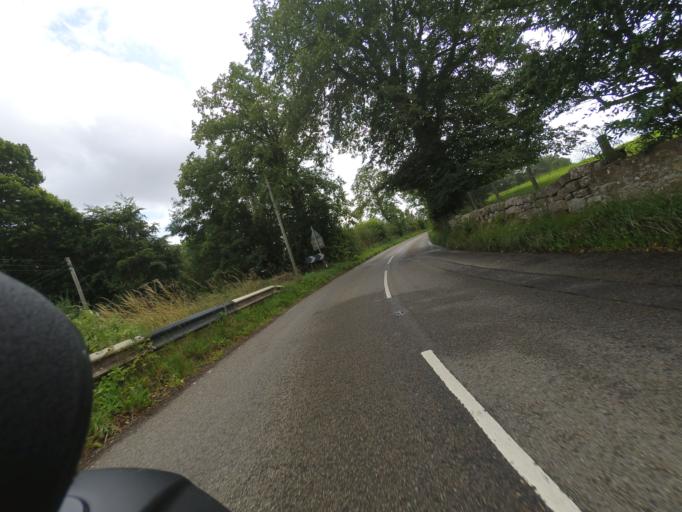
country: GB
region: Scotland
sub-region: Highland
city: Tain
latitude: 57.7442
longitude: -4.0736
